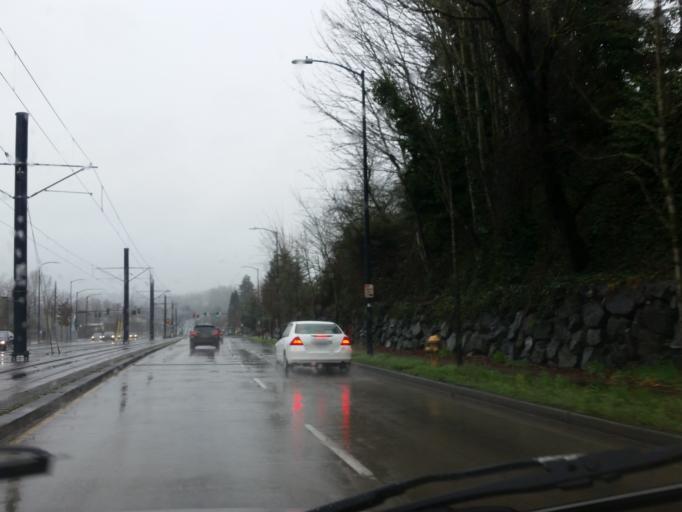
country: US
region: Washington
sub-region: King County
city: Seattle
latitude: 47.5703
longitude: -122.2968
